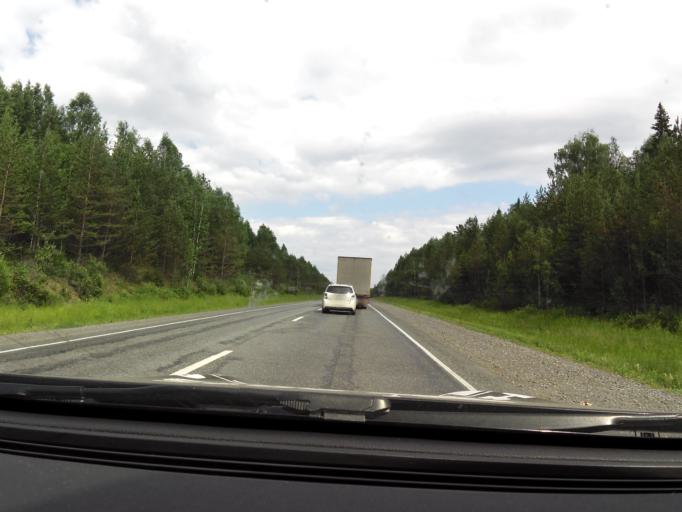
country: RU
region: Sverdlovsk
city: Nizhniye Sergi
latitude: 56.8247
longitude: 59.2769
